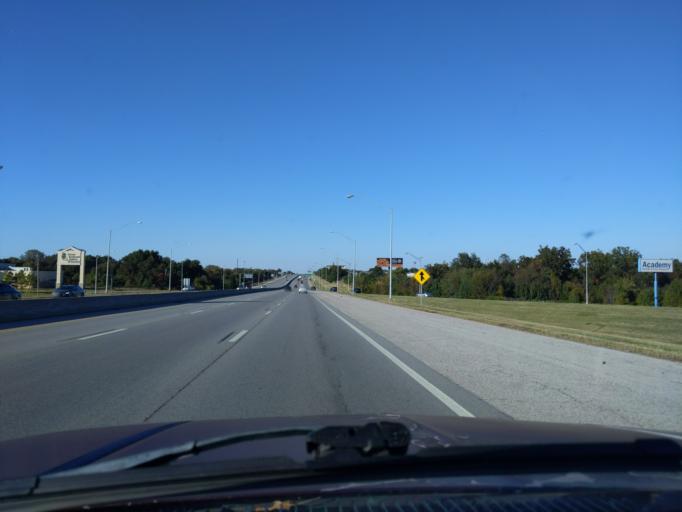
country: US
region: Oklahoma
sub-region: Tulsa County
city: Broken Arrow
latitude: 36.0486
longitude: -95.8591
